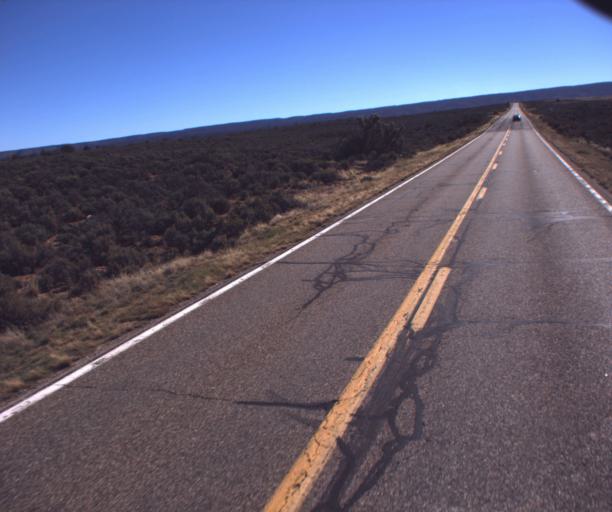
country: US
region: Arizona
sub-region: Coconino County
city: Fredonia
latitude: 36.8786
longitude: -112.3362
